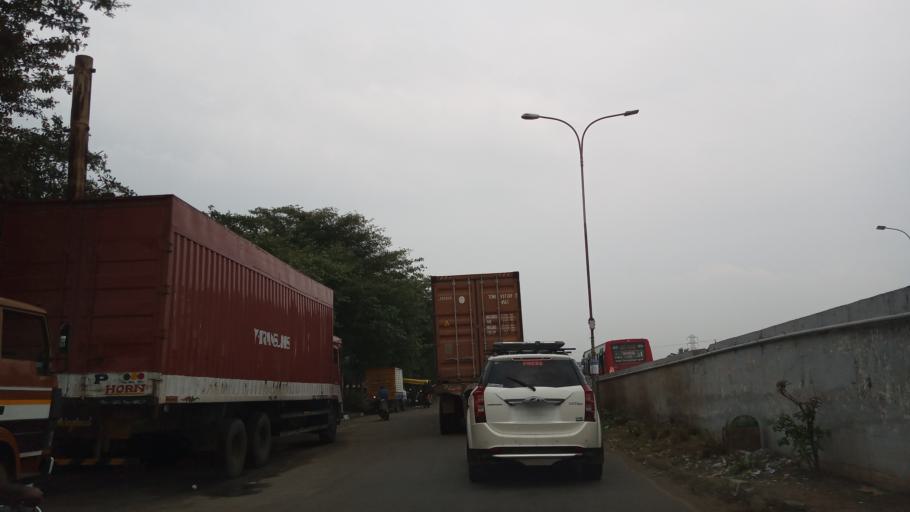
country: IN
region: Tamil Nadu
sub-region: Kancheepuram
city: Madambakkam
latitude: 12.8528
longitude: 79.9452
